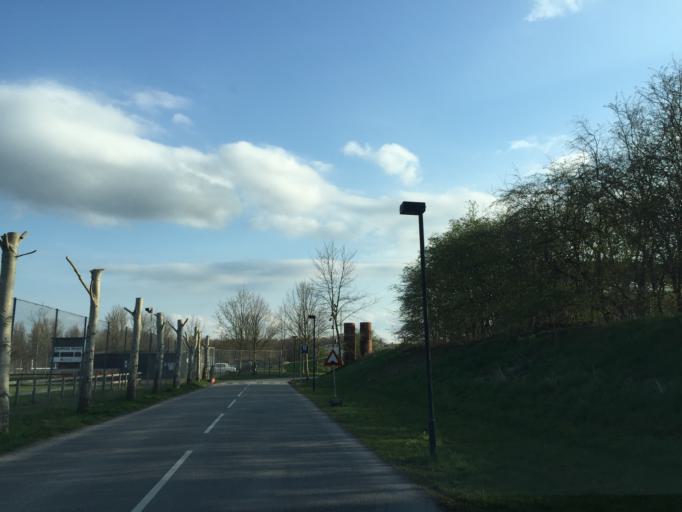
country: DK
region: South Denmark
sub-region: Odense Kommune
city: Neder Holluf
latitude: 55.3712
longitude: 10.4327
